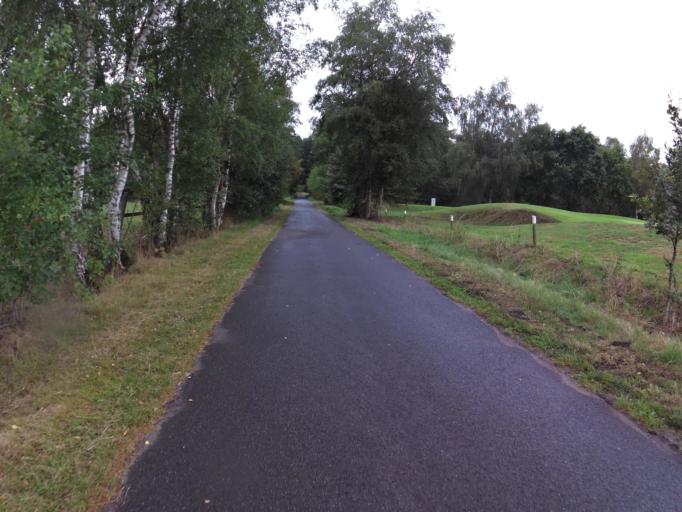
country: DE
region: Lower Saxony
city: Hamersen
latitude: 53.2696
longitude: 9.4776
